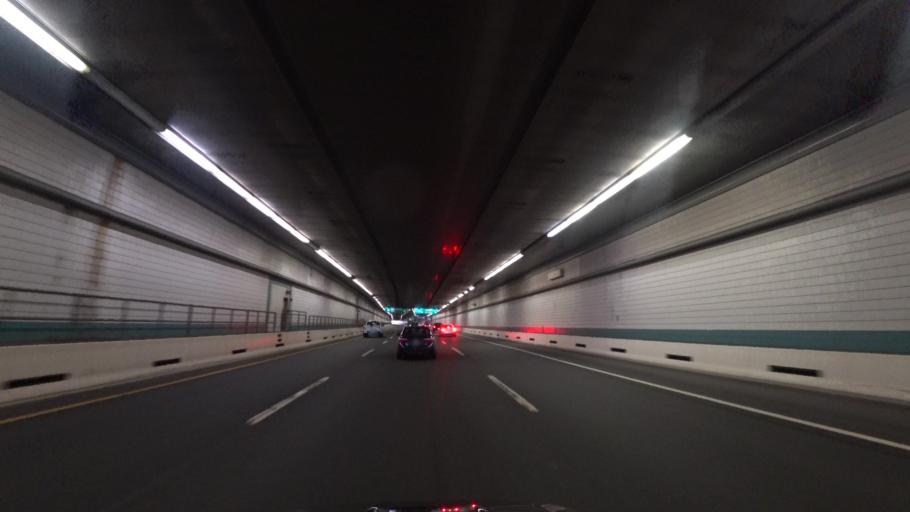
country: US
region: Massachusetts
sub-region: Suffolk County
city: Boston
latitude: 42.3592
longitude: -71.0278
